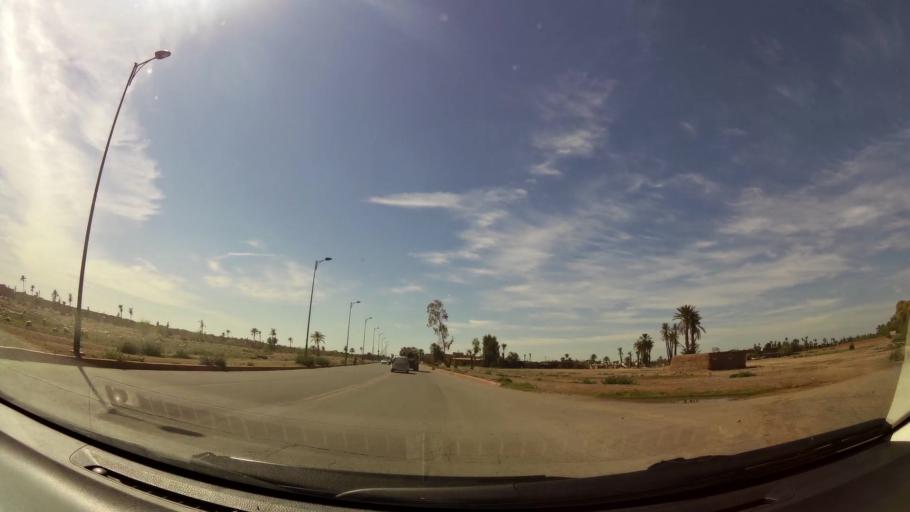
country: MA
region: Marrakech-Tensift-Al Haouz
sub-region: Marrakech
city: Marrakesh
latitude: 31.6185
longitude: -7.9580
